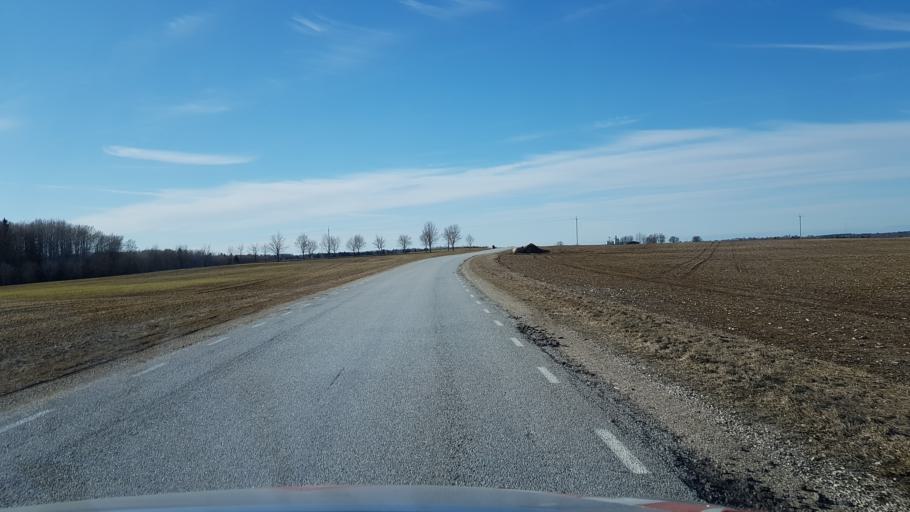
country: EE
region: Laeaene-Virumaa
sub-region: Kadrina vald
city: Kadrina
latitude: 59.2849
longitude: 26.1808
